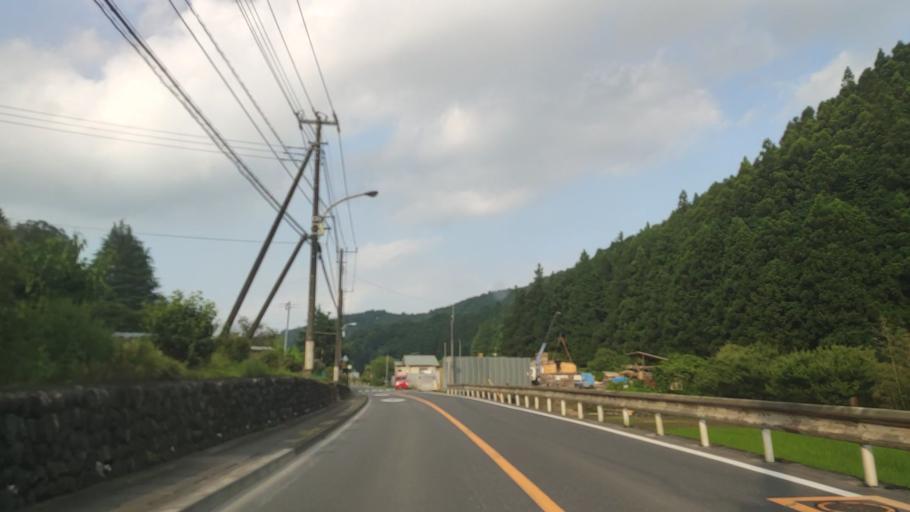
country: JP
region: Tokyo
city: Ome
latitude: 35.8233
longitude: 139.2530
